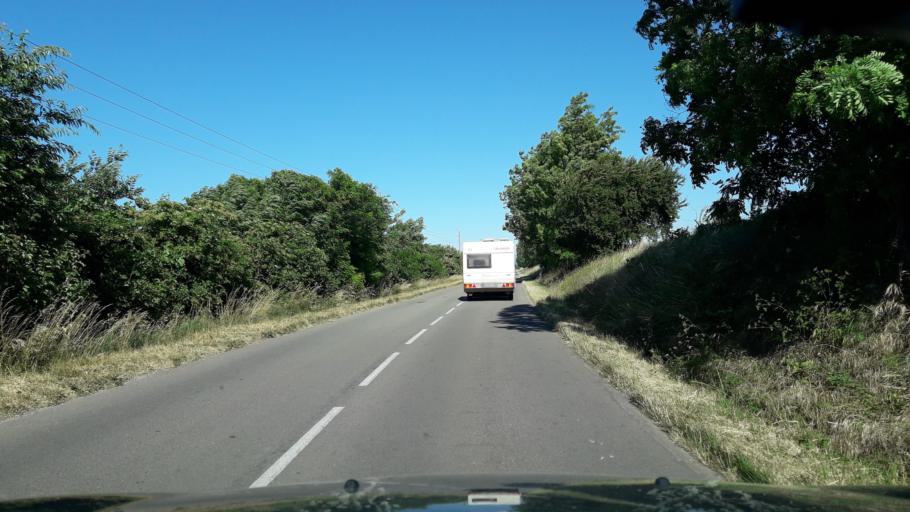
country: FR
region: Rhone-Alpes
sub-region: Departement de la Drome
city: Loriol-sur-Drome
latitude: 44.7572
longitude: 4.8401
